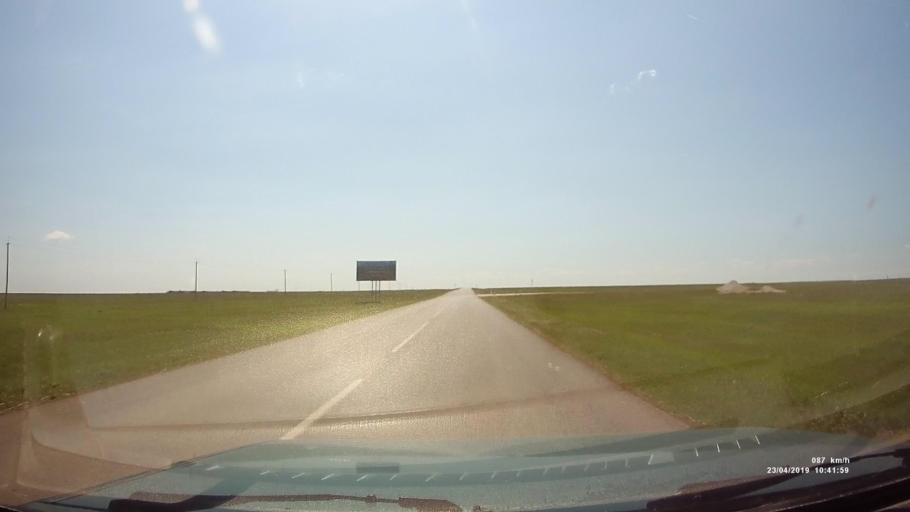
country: RU
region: Kalmykiya
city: Yashalta
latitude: 46.4878
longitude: 42.6409
